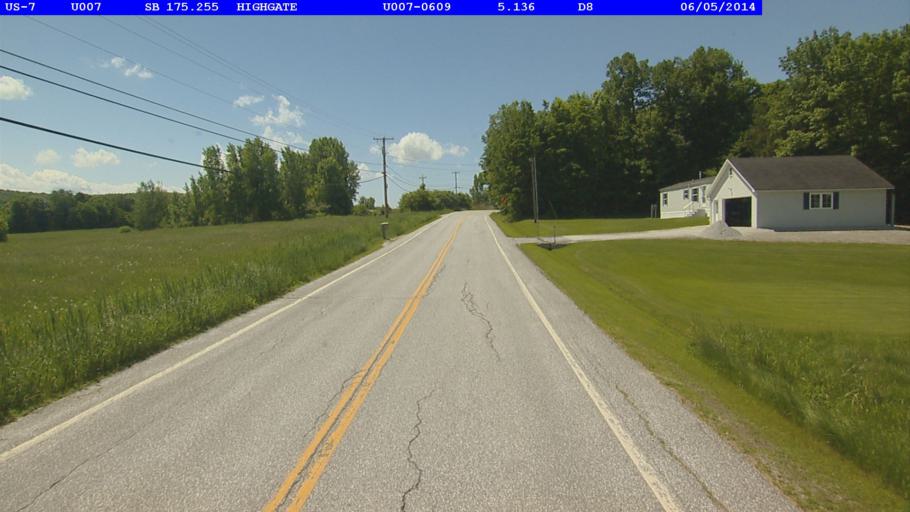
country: US
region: Vermont
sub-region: Franklin County
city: Swanton
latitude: 44.9990
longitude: -73.0786
